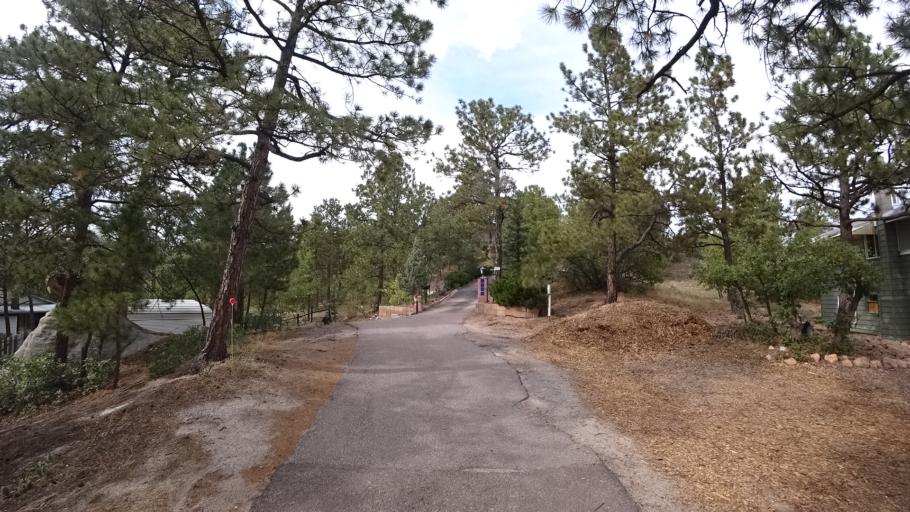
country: US
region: Colorado
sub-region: El Paso County
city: Cimarron Hills
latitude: 38.8755
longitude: -104.7616
